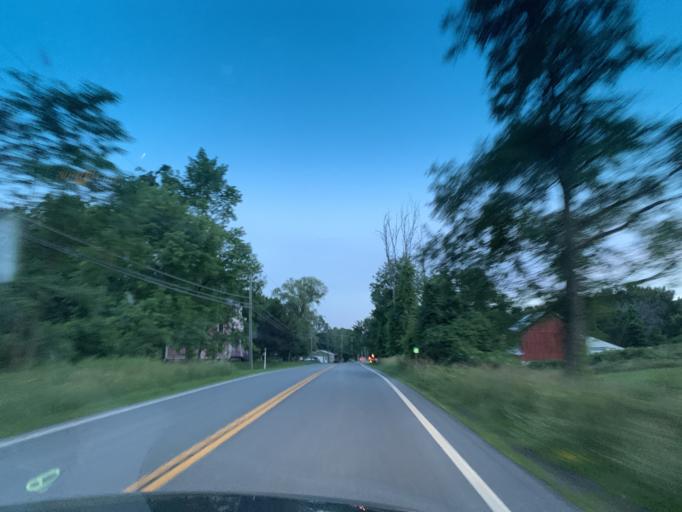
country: US
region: New York
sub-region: Chenango County
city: New Berlin
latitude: 42.6383
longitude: -75.3315
